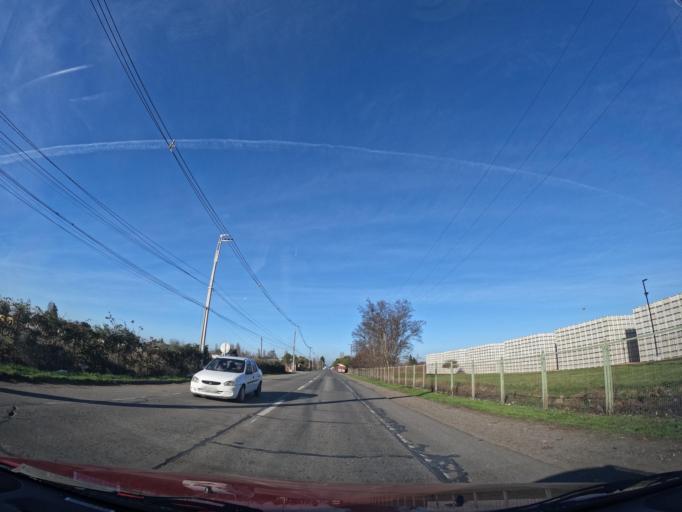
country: CL
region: Maule
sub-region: Provincia de Linares
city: San Javier
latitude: -35.5739
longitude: -71.6754
